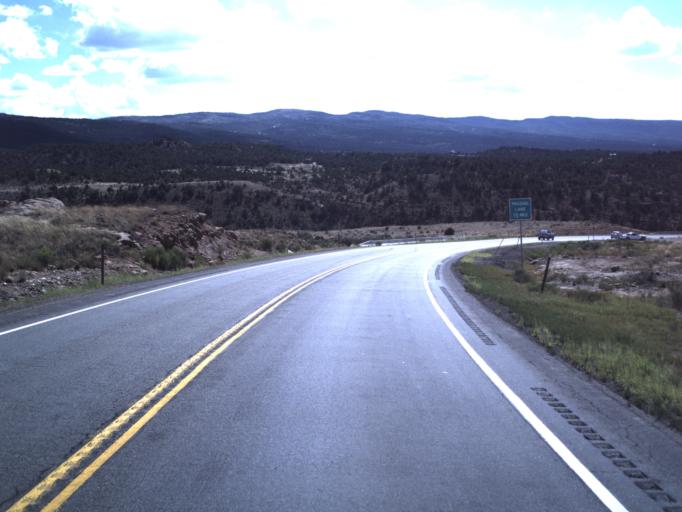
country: US
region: Utah
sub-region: Duchesne County
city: Duchesne
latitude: 40.2001
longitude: -110.7762
